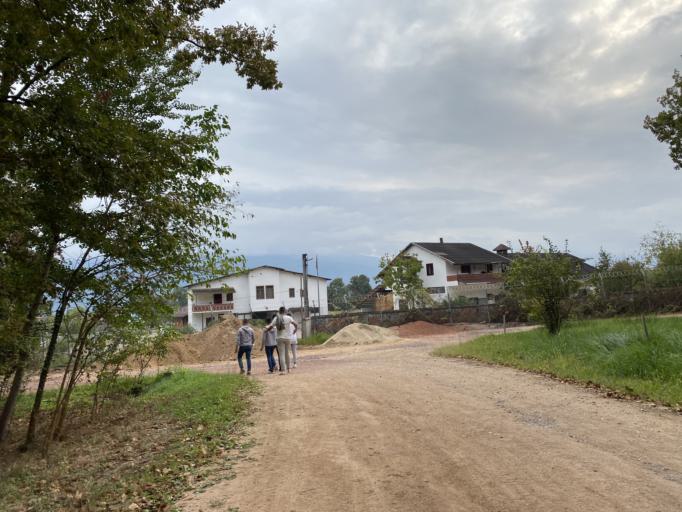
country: TR
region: Kocaeli
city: Derbent
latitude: 40.7358
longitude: 30.1600
